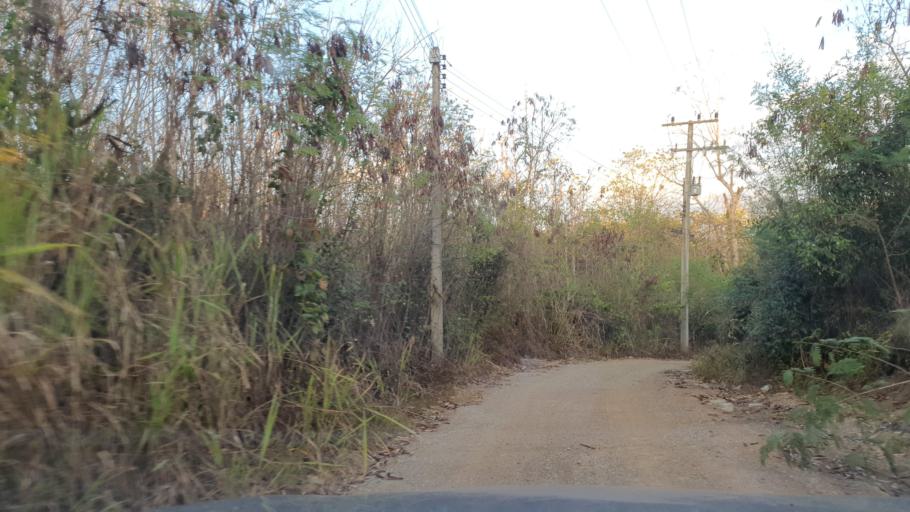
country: TH
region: Chiang Mai
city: Hang Dong
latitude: 18.7319
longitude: 98.8819
